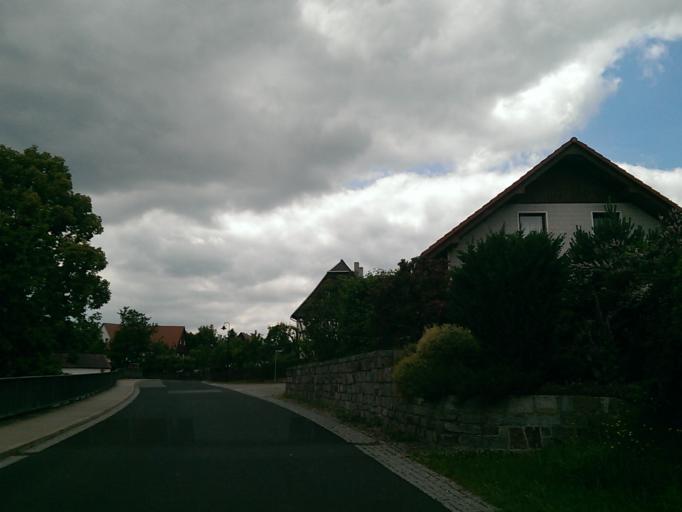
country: DE
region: Saxony
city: Bertsdorf-Hoernitz
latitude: 50.8863
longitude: 14.7356
